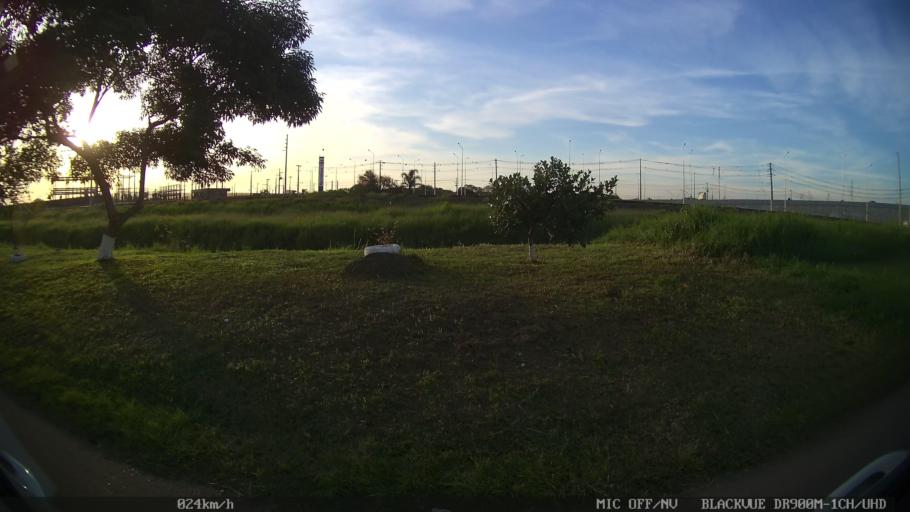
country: BR
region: Parana
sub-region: Pinhais
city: Pinhais
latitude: -25.4386
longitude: -49.1647
